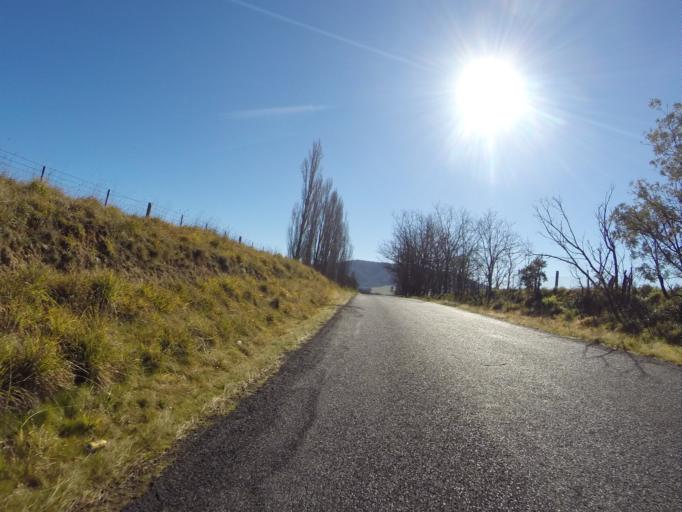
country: AU
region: New South Wales
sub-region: Oberon
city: Oberon
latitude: -33.5534
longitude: 149.8720
